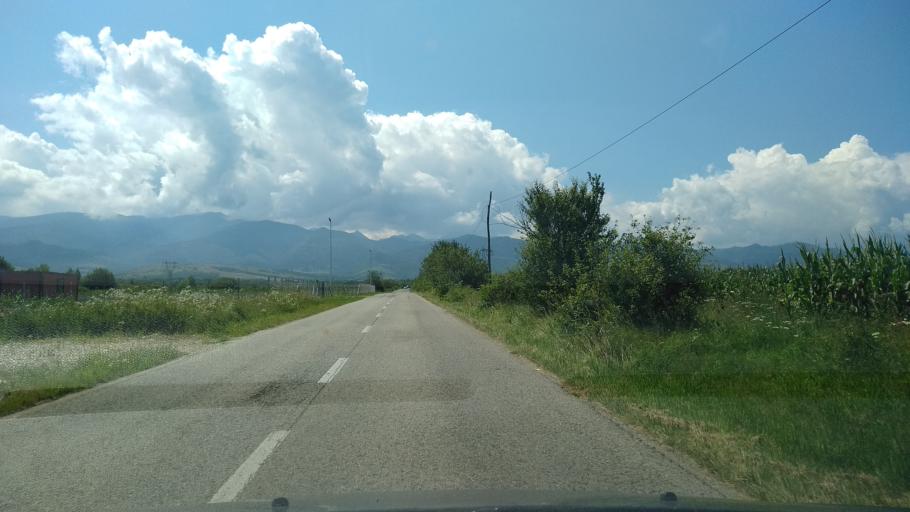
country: RO
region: Hunedoara
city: Salasu de Sus
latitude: 45.5254
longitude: 22.9646
